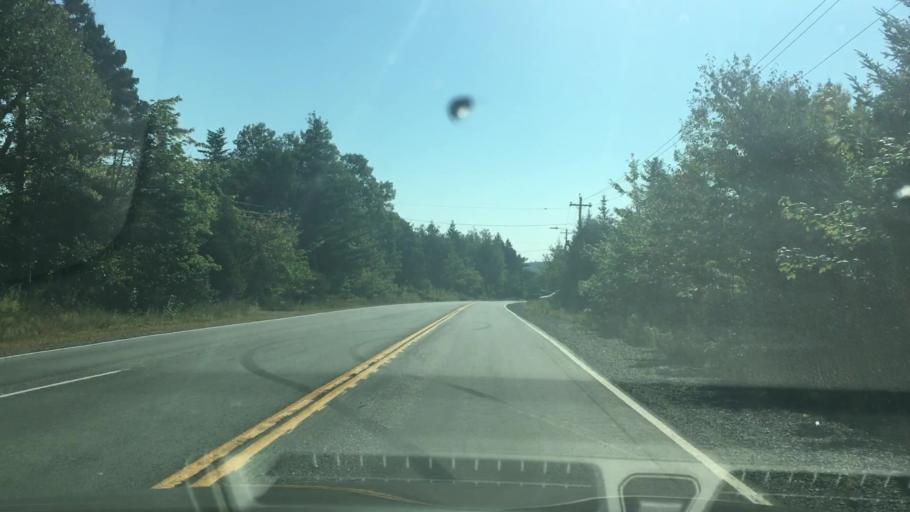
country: CA
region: Nova Scotia
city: Cole Harbour
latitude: 44.7780
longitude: -63.0753
